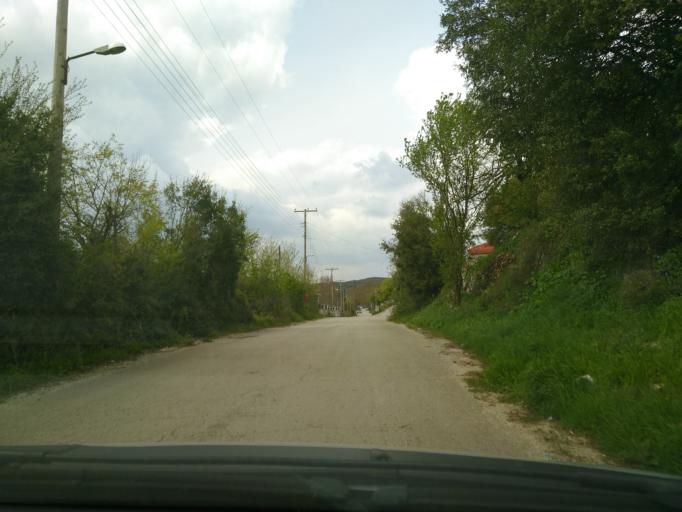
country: GR
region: Epirus
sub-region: Nomos Ioanninon
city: Asprangeloi
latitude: 39.7771
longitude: 20.6886
